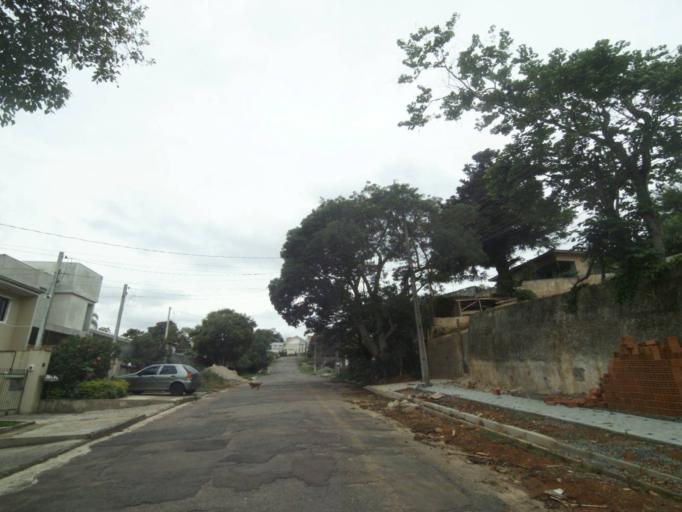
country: BR
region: Parana
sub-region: Curitiba
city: Curitiba
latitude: -25.3926
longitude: -49.2935
